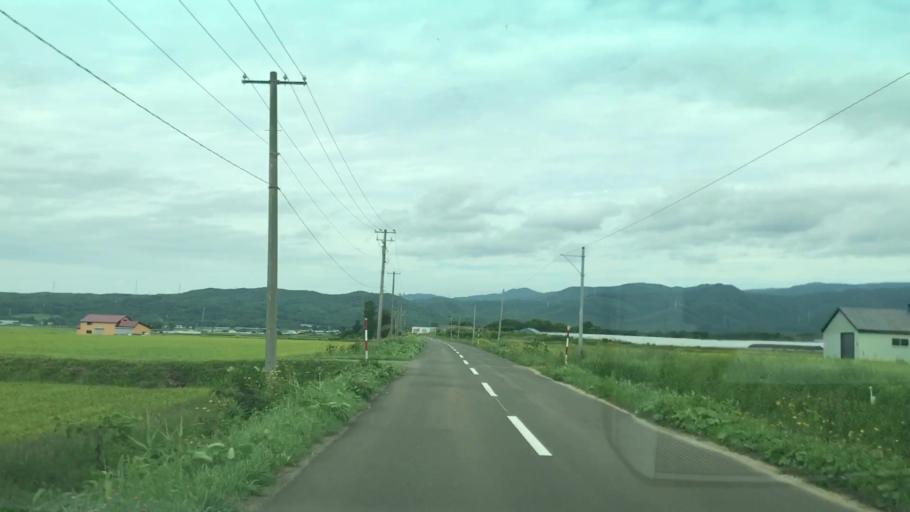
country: JP
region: Hokkaido
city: Iwanai
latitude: 43.0217
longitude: 140.5730
